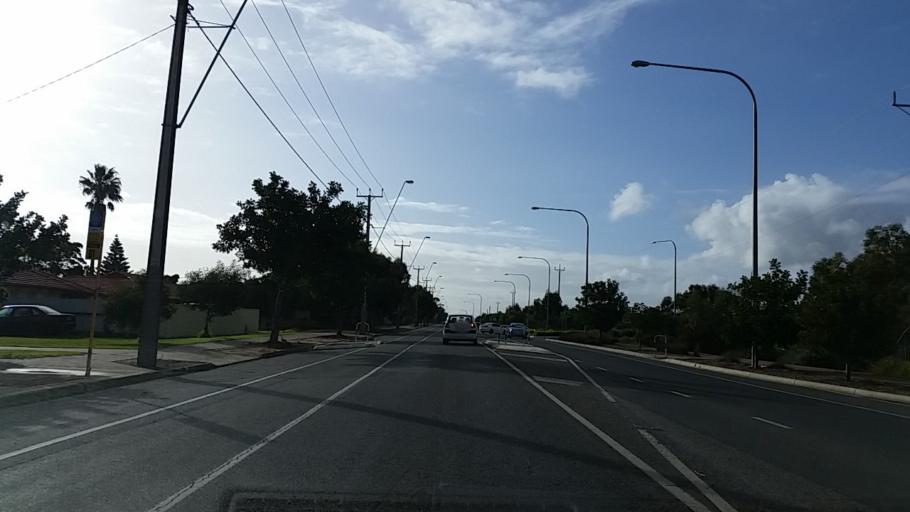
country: AU
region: South Australia
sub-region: Onkaparinga
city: Seaford
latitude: -35.1770
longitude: 138.4764
